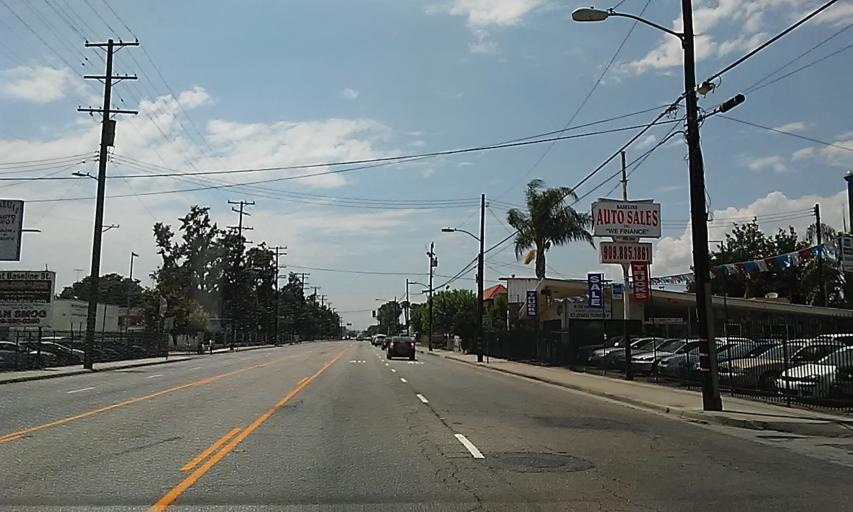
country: US
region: California
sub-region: San Bernardino County
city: San Bernardino
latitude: 34.1214
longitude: -117.2718
